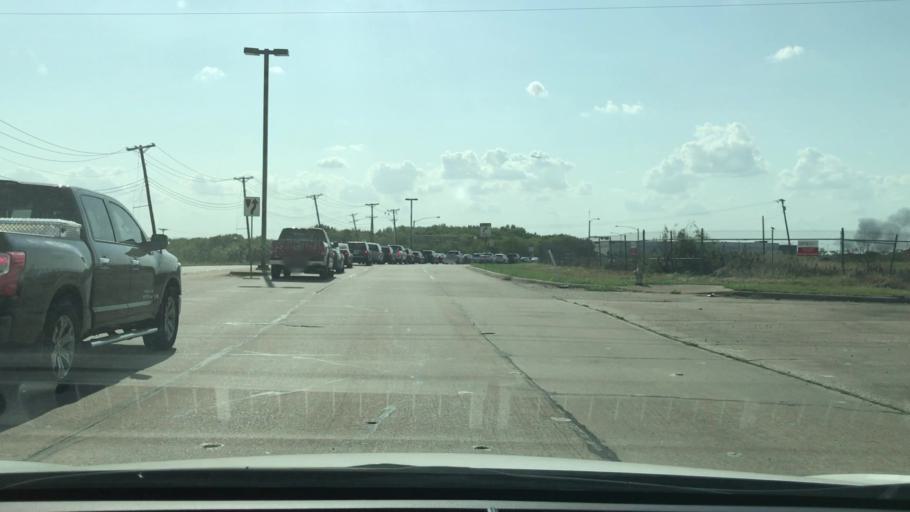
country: US
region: Texas
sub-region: Tarrant County
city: Euless
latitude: 32.8668
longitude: -97.0133
